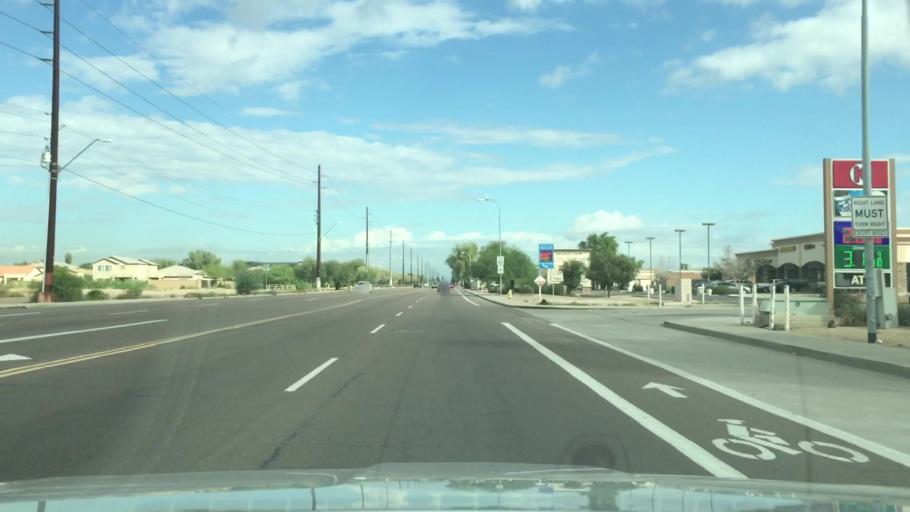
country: US
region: Arizona
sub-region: Maricopa County
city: Tolleson
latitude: 33.4657
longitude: -112.2552
